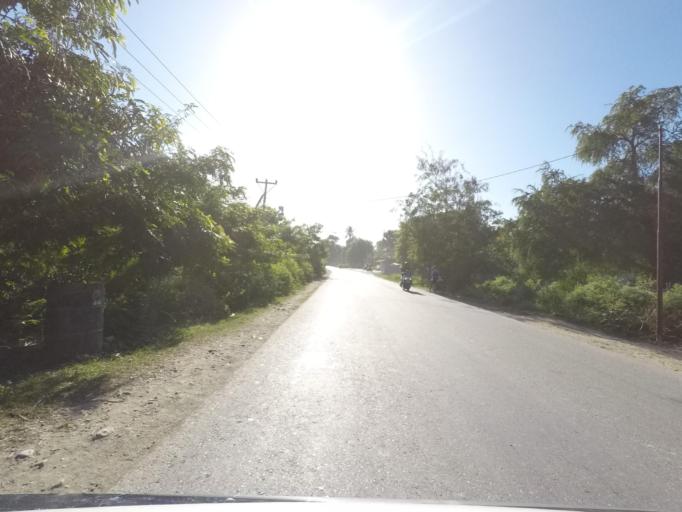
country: TL
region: Dili
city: Dili
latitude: -8.5548
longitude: 125.6564
